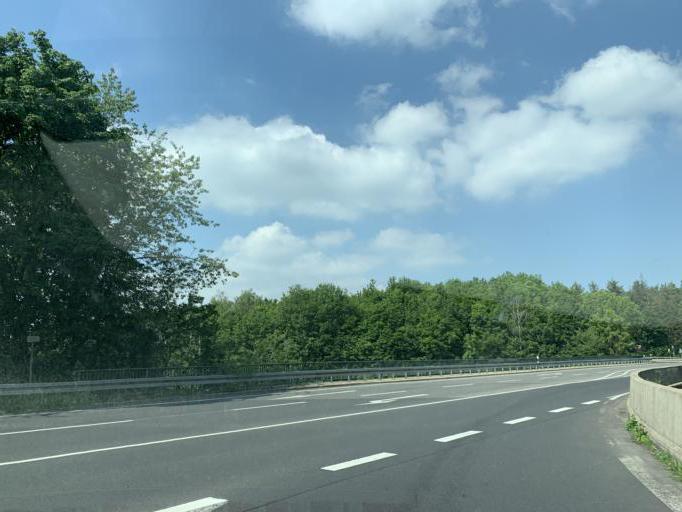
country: DE
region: North Rhine-Westphalia
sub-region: Regierungsbezirk Koln
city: Weilerswist
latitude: 50.7958
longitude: 6.8699
